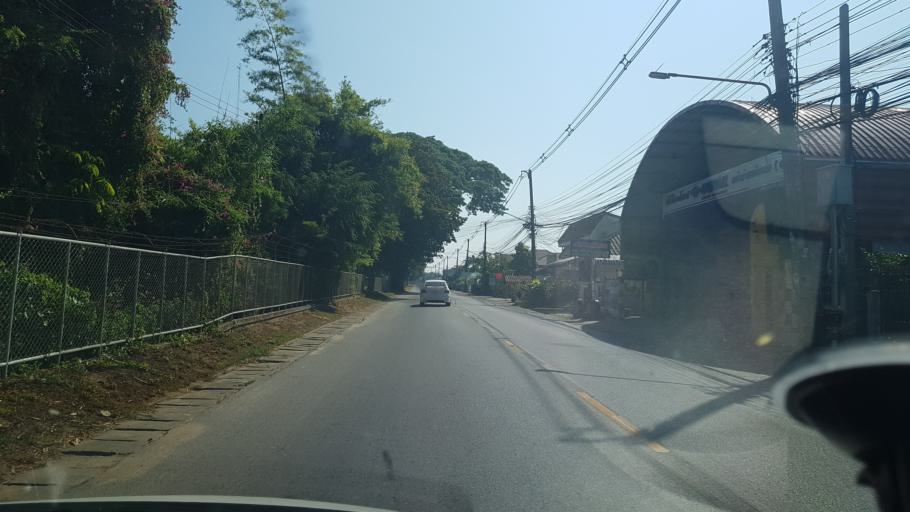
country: TH
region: Chiang Rai
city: Chiang Rai
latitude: 19.9079
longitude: 99.8047
